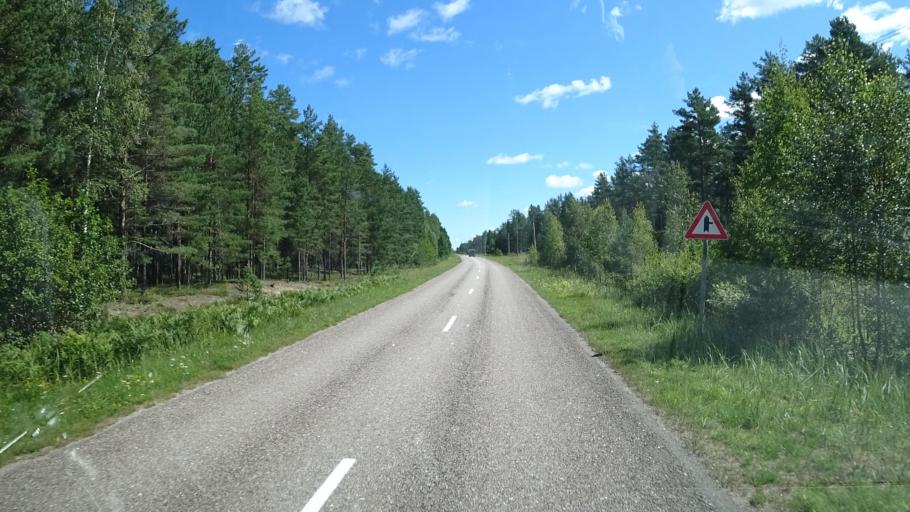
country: LV
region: Ventspils
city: Ventspils
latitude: 57.5670
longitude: 21.8603
